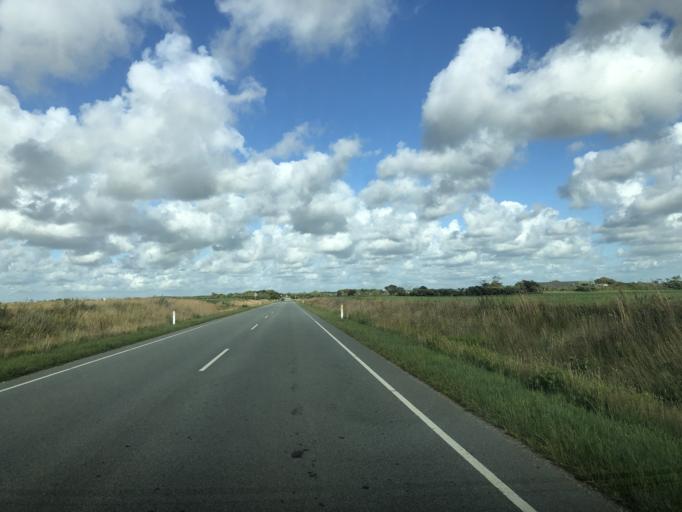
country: DK
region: Central Jutland
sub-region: Lemvig Kommune
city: Lemvig
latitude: 56.4926
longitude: 8.2217
